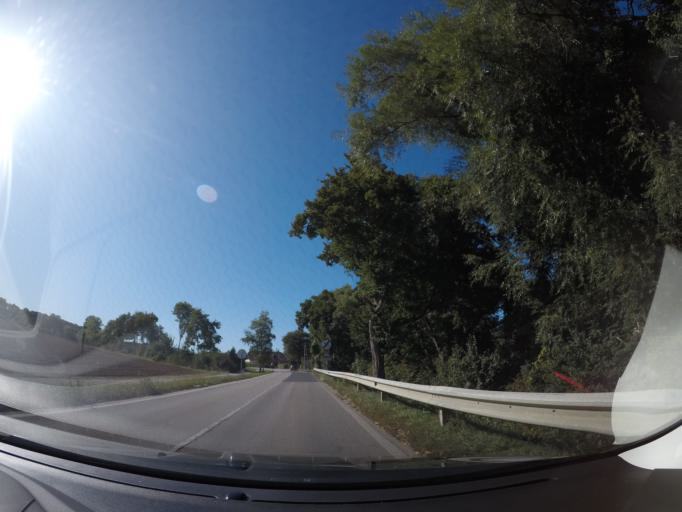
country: AT
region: Lower Austria
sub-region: Politischer Bezirk Modling
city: Laab im Walde
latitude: 48.1513
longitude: 16.1859
